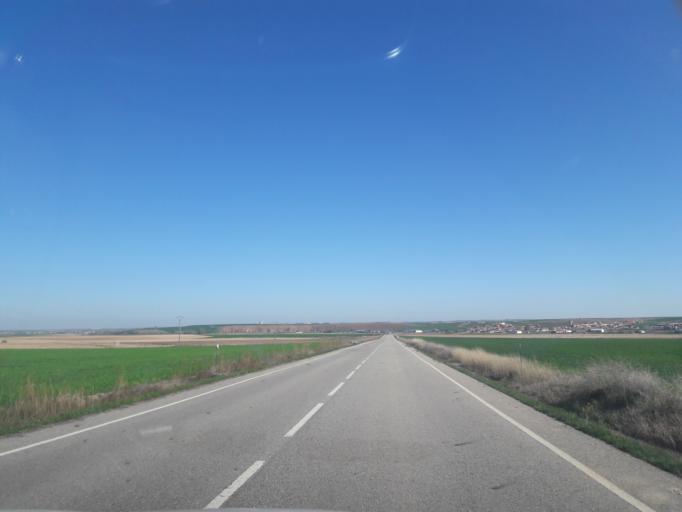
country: ES
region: Castille and Leon
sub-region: Provincia de Salamanca
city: Mancera de Abajo
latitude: 40.8259
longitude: -5.2084
